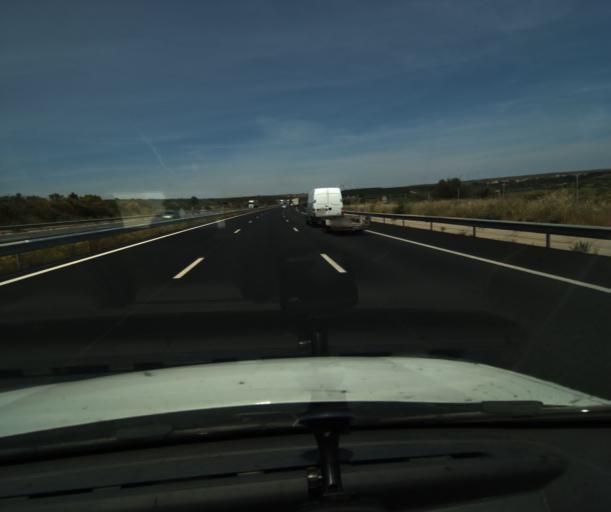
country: FR
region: Languedoc-Roussillon
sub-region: Departement de l'Aude
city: Sigean
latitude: 42.9678
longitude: 2.9690
